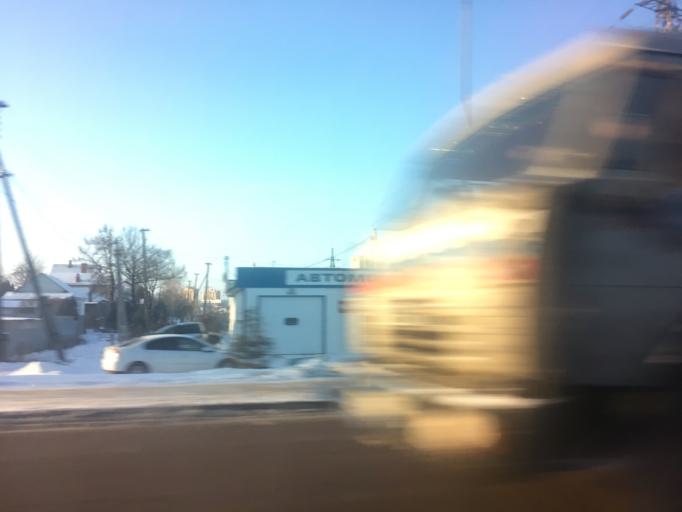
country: RU
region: Tula
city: Tula
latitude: 54.2035
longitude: 37.6791
